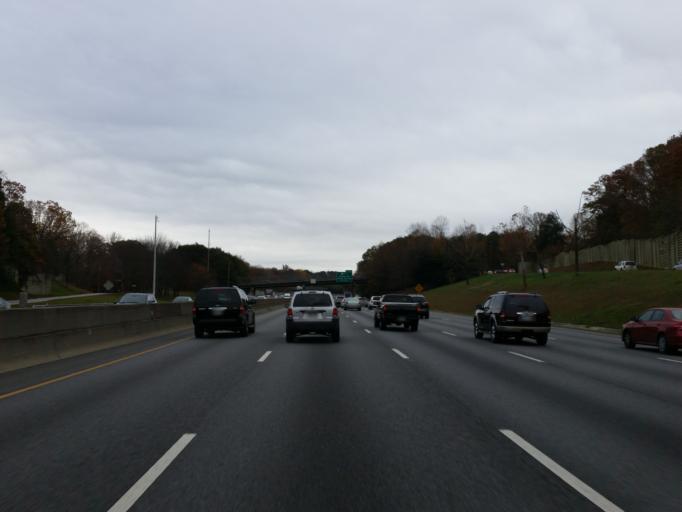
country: US
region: Georgia
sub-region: Fulton County
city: Sandy Springs
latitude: 33.9159
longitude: -84.4100
